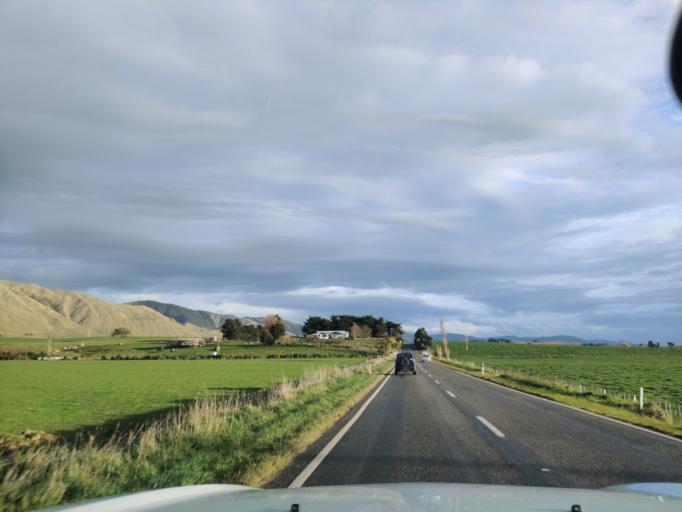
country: NZ
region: Manawatu-Wanganui
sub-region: Horowhenua District
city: Foxton
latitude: -40.5027
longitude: 175.4872
